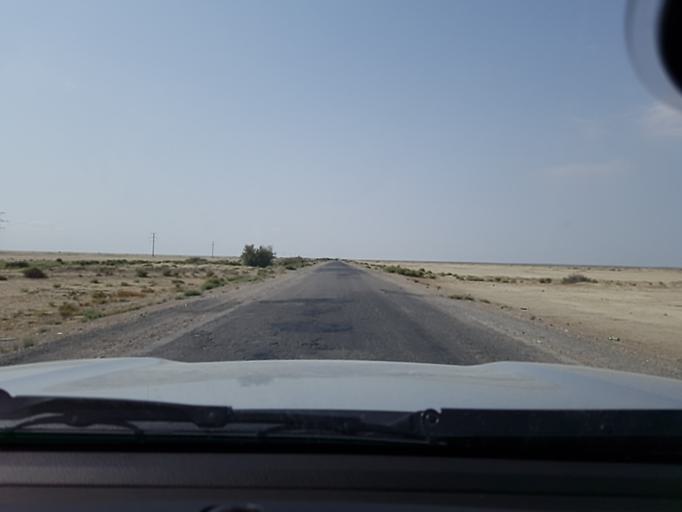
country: TM
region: Balkan
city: Gumdag
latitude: 38.9823
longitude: 54.5872
